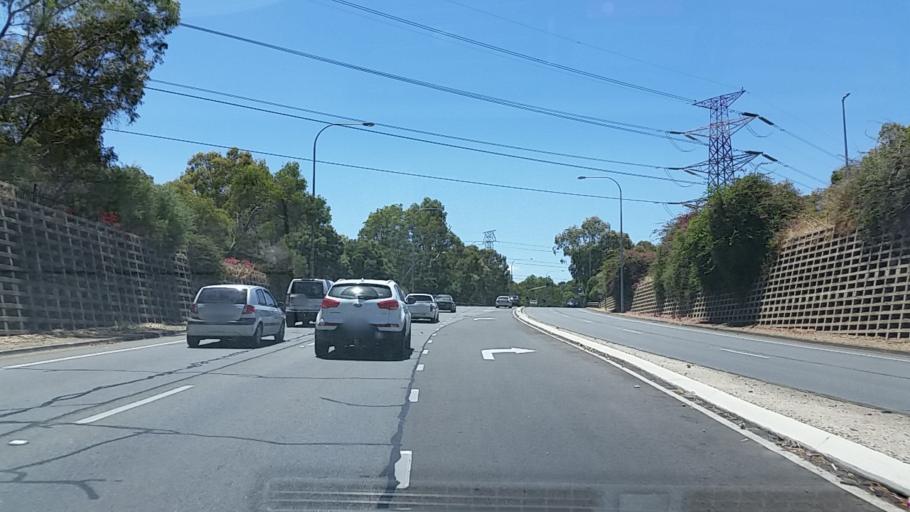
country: AU
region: South Australia
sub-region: Salisbury
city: Salisbury
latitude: -34.7597
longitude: 138.6426
